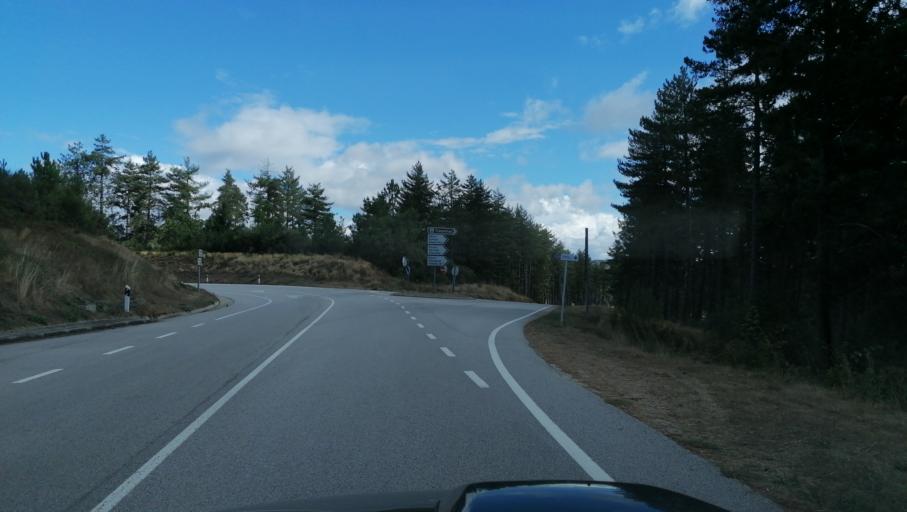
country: PT
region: Vila Real
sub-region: Vila Pouca de Aguiar
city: Vila Pouca de Aguiar
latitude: 41.5177
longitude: -7.5968
